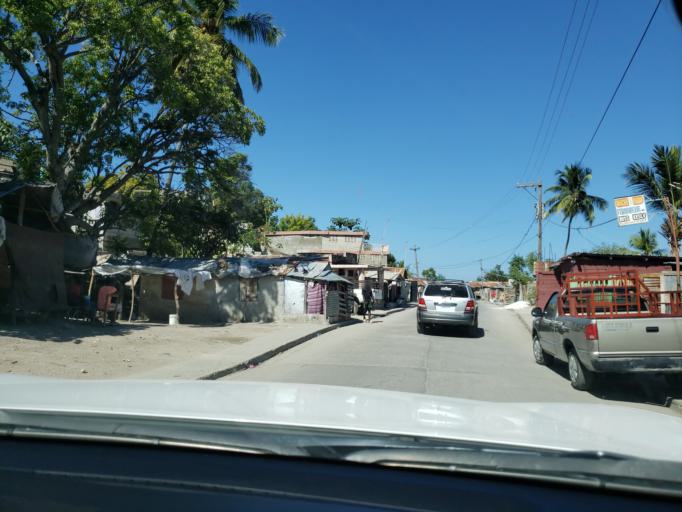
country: HT
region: Nippes
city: Miragoane
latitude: 18.4431
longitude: -73.0944
